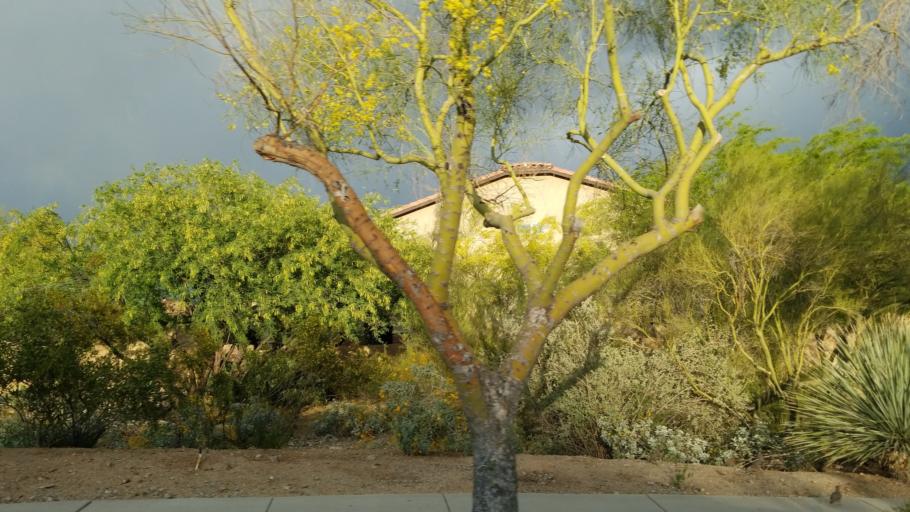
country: US
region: Arizona
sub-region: Maricopa County
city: Paradise Valley
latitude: 33.5898
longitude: -112.0565
